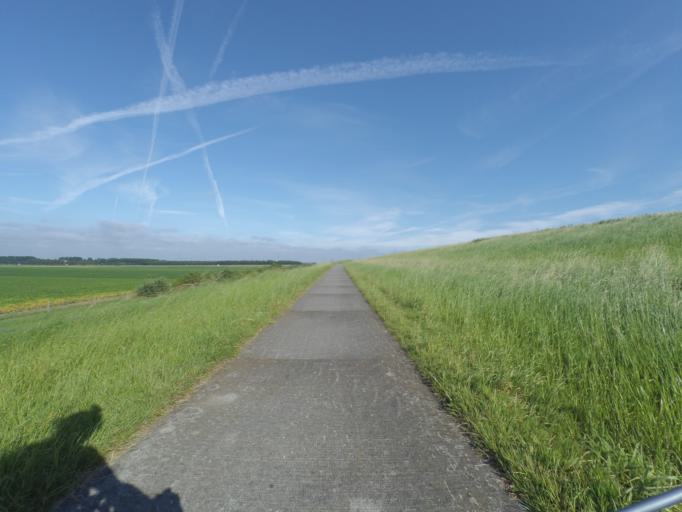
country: NL
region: Flevoland
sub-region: Gemeente Lelystad
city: Lelystad
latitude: 52.4381
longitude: 5.4453
